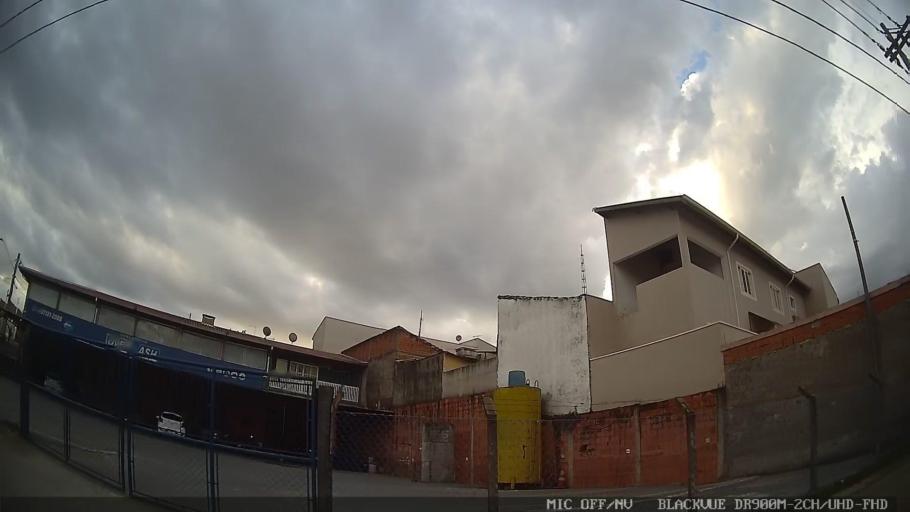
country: BR
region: Sao Paulo
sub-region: Indaiatuba
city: Indaiatuba
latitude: -23.1286
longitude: -47.2343
